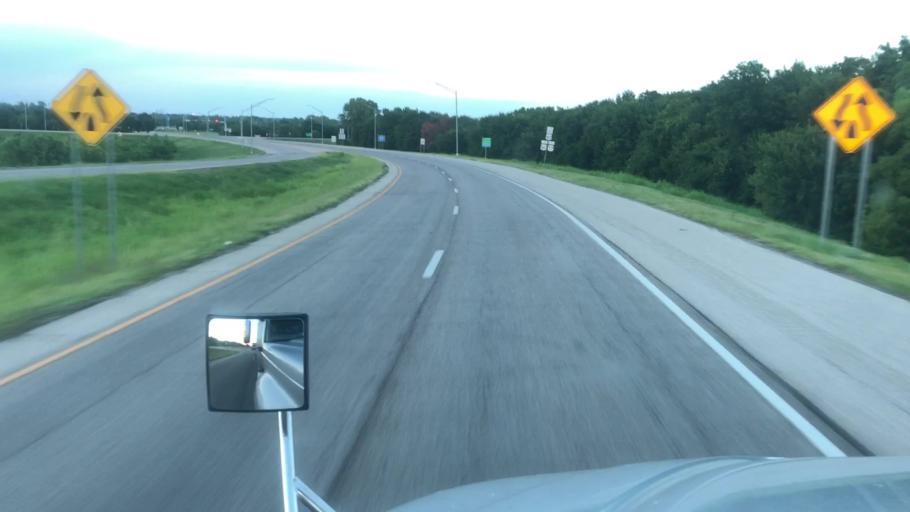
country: US
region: Oklahoma
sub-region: Kay County
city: Ponca City
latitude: 36.6772
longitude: -97.0710
